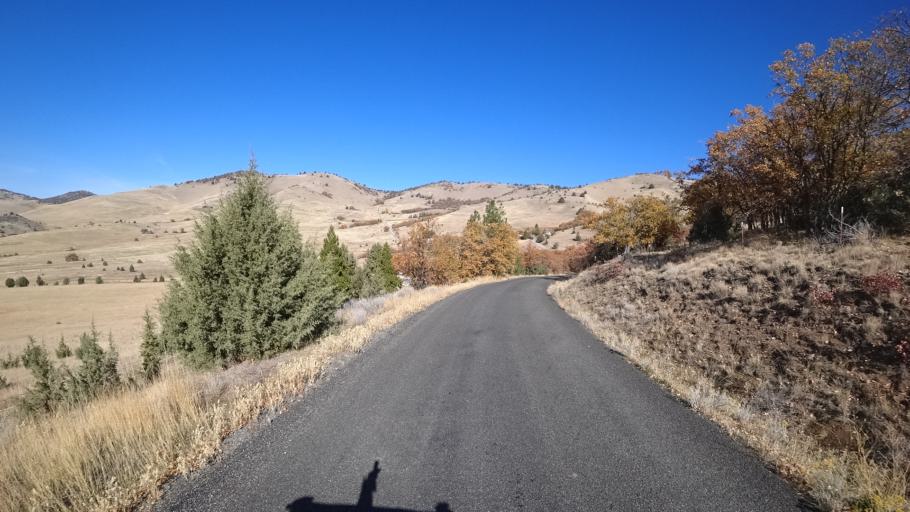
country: US
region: California
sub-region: Siskiyou County
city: Montague
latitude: 41.8286
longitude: -122.3435
